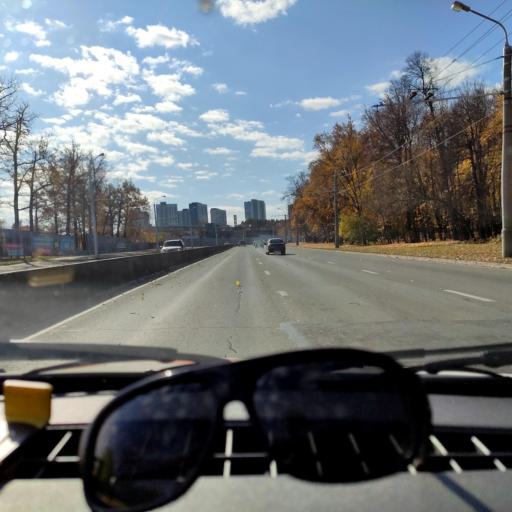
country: RU
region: Bashkortostan
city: Ufa
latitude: 54.7303
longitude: 56.0244
